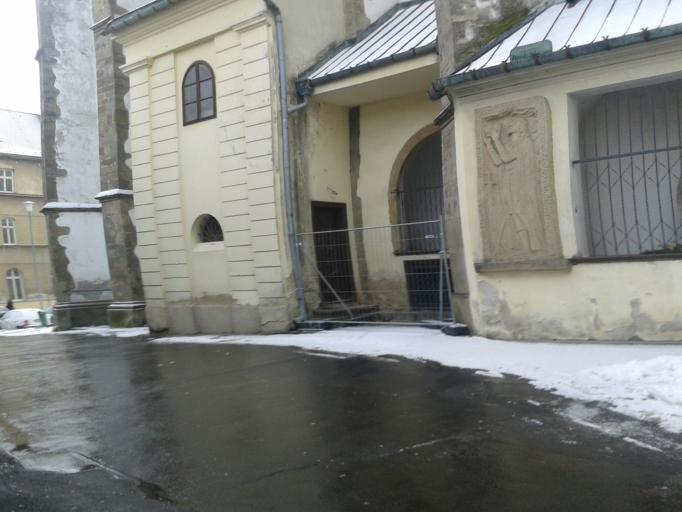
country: CZ
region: Olomoucky
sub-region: Okres Prostejov
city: Prostejov
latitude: 49.4720
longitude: 17.1121
